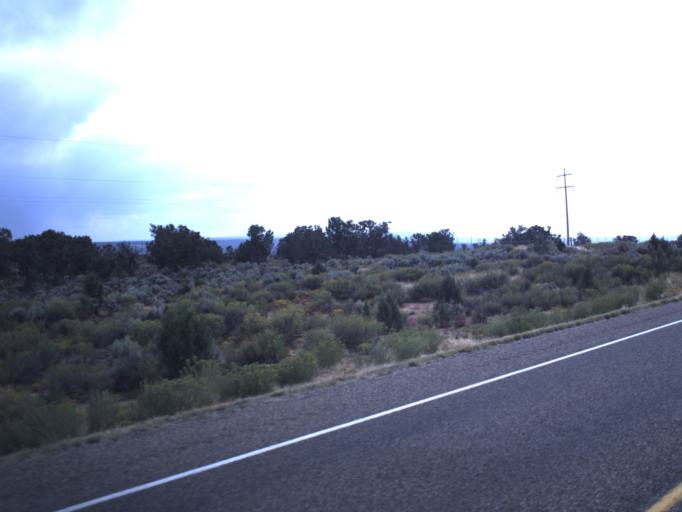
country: US
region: Utah
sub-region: Kane County
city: Kanab
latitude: 37.0729
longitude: -112.1721
